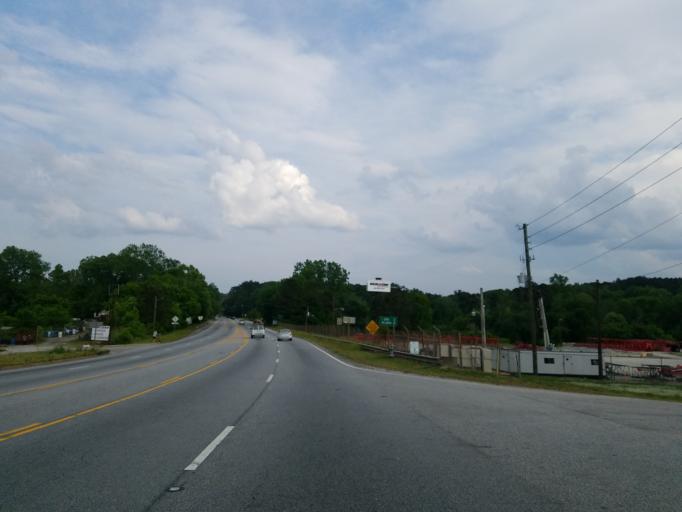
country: US
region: Georgia
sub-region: Cobb County
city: Mableton
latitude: 33.7967
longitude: -84.5103
